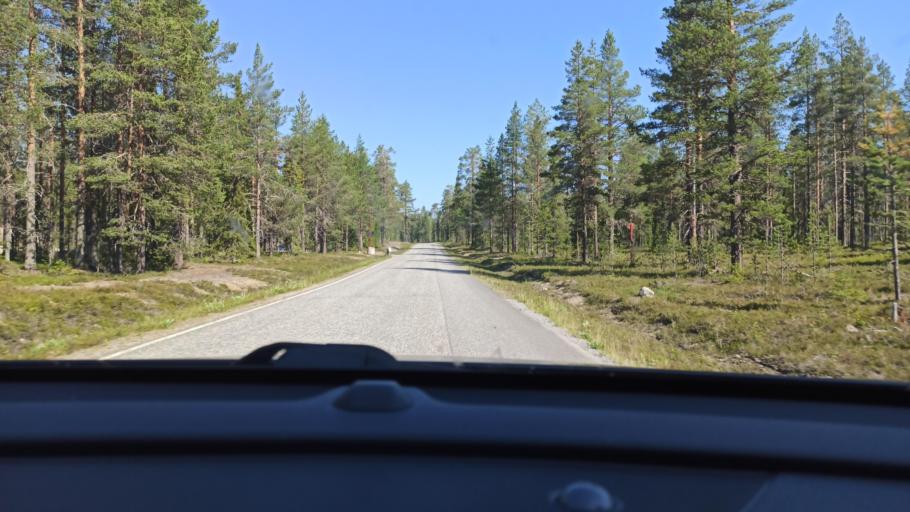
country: FI
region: Lapland
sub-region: Tunturi-Lappi
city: Kolari
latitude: 67.6573
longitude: 24.1649
